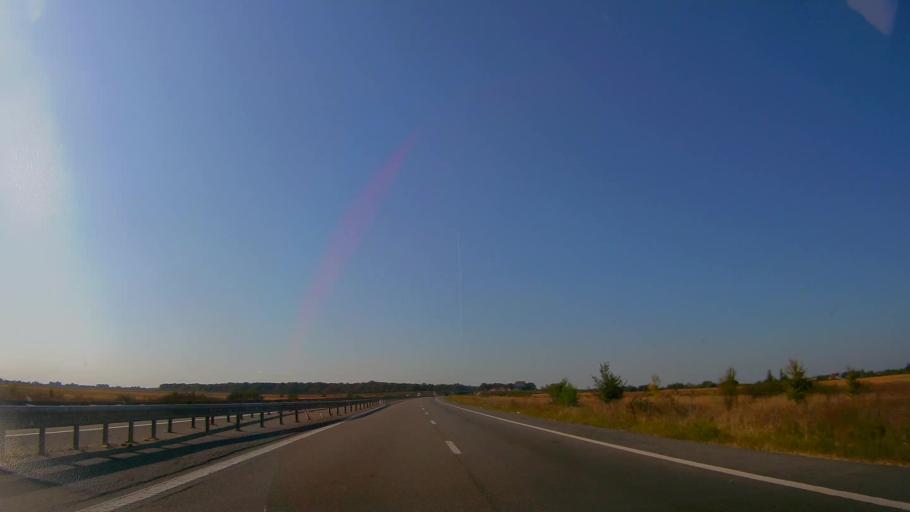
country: RO
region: Dambovita
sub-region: Comuna Corbii Mari
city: Grozavesti
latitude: 44.5723
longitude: 25.4769
